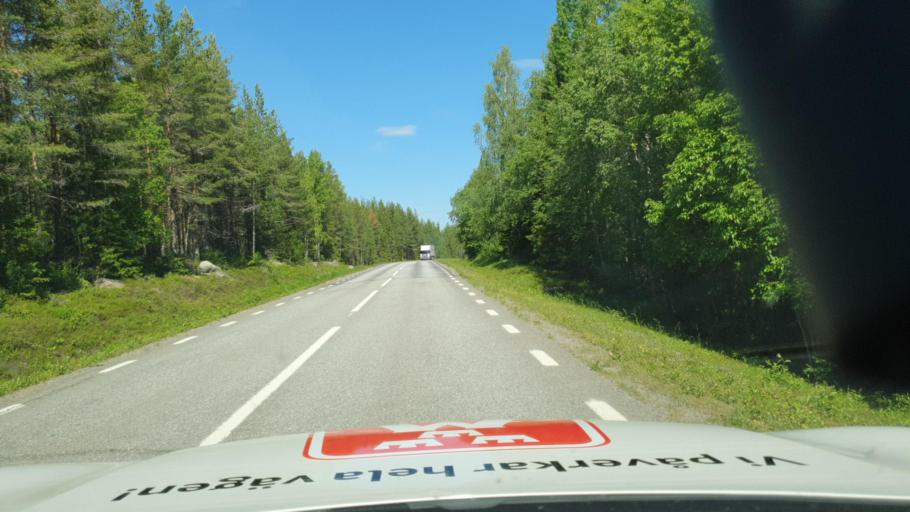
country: SE
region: Vaesterbotten
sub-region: Skelleftea Kommun
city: Boliden
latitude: 64.8364
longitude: 20.3690
